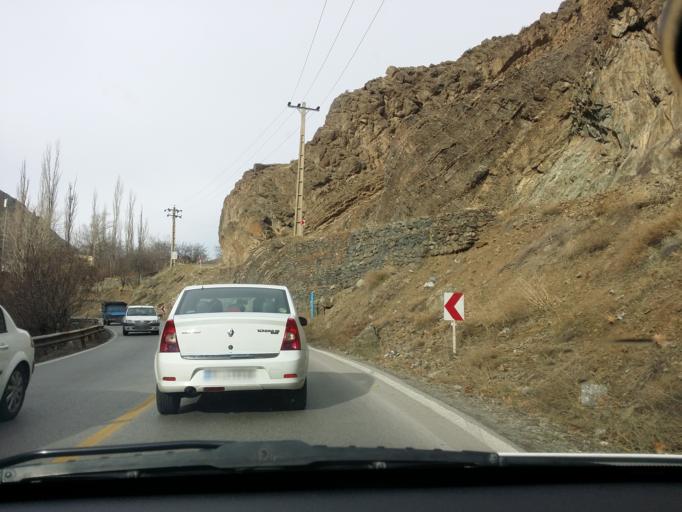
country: IR
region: Tehran
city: Tajrish
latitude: 36.0226
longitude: 51.2636
